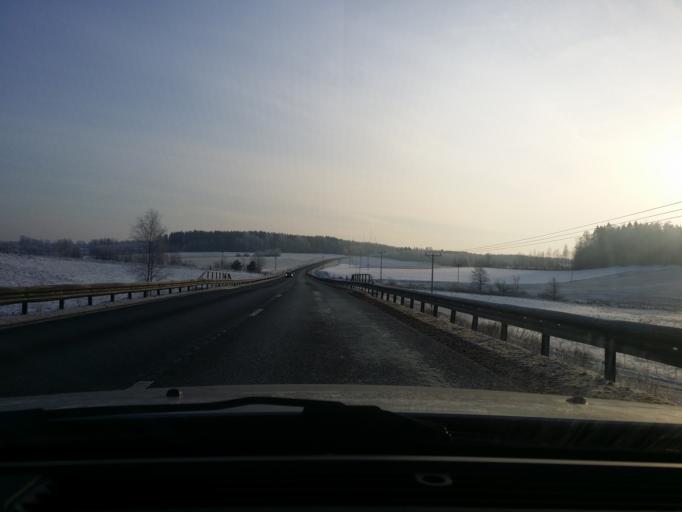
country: SE
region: OErebro
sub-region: Lindesbergs Kommun
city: Lindesberg
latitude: 59.5887
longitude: 15.1892
